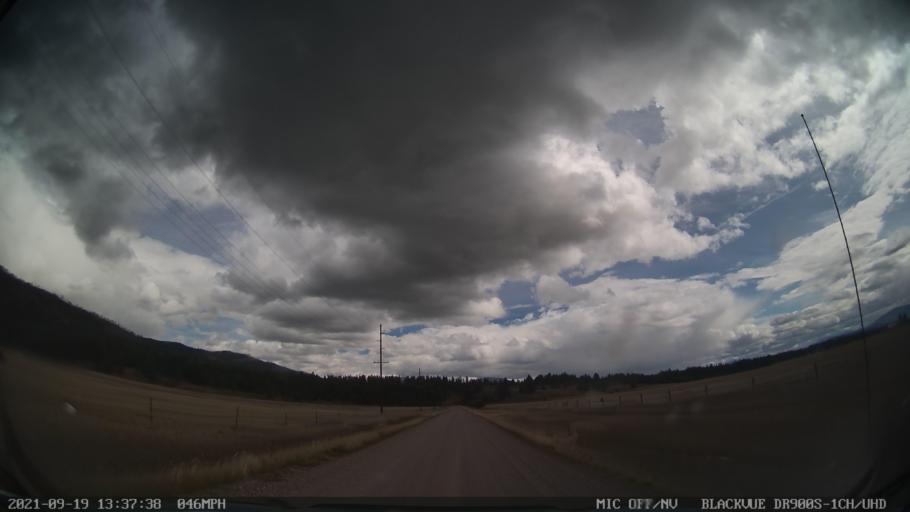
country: US
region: Montana
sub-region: Missoula County
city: Seeley Lake
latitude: 47.1066
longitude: -113.2802
